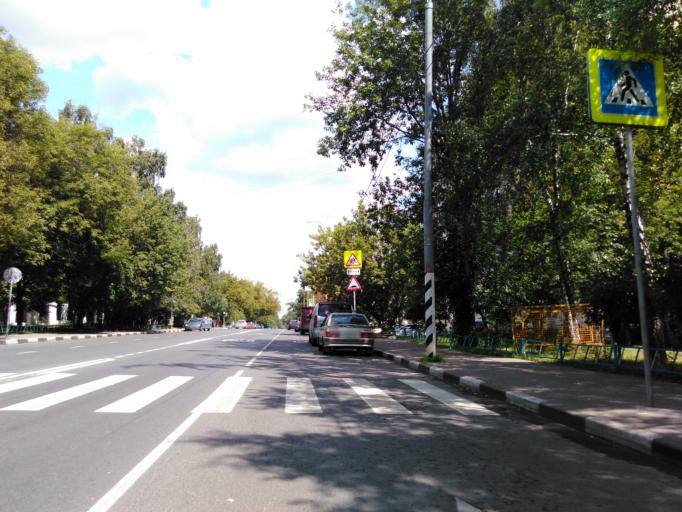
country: RU
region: Moscow
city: Kotlovka
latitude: 55.6779
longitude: 37.6017
